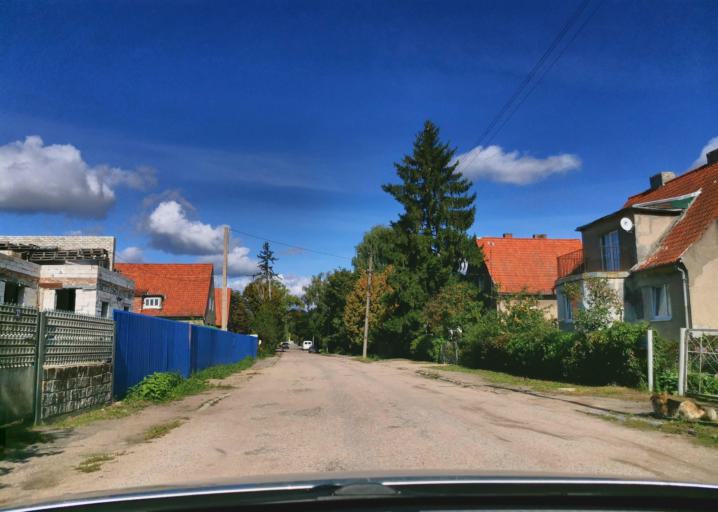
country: RU
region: Kaliningrad
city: Chernyakhovsk
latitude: 54.6348
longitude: 21.8407
